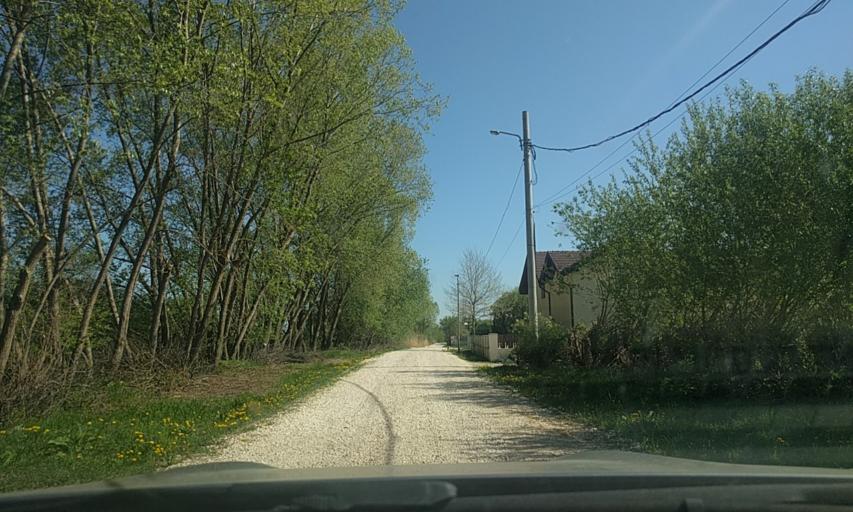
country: RO
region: Brasov
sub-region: Comuna Bod
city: Colonia Bod
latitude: 45.7200
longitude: 25.5664
